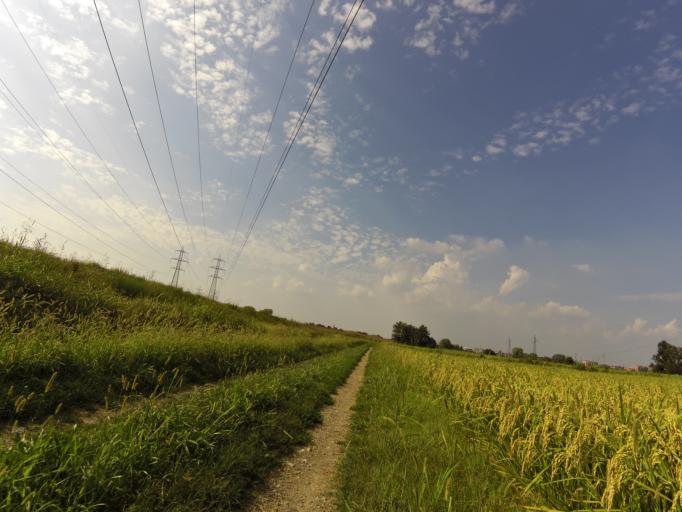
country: IT
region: Lombardy
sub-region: Citta metropolitana di Milano
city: Civesio
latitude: 45.3888
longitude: 9.2754
